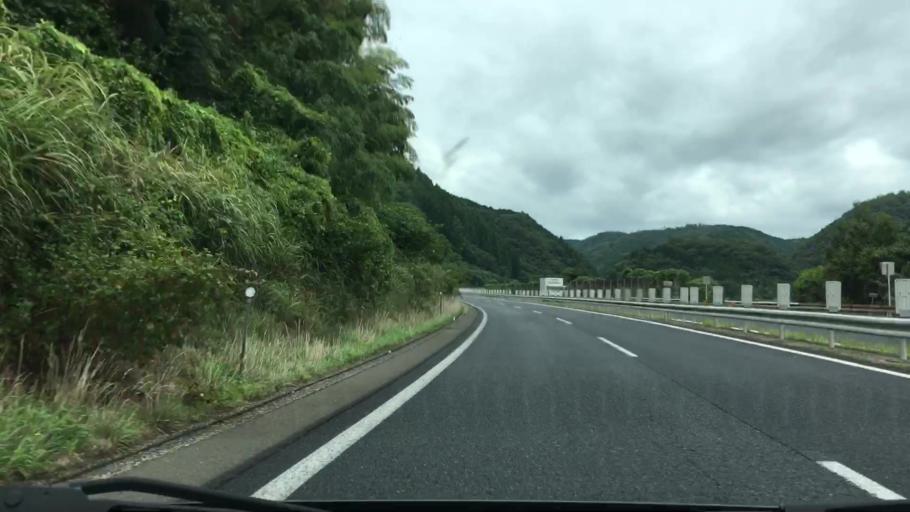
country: JP
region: Hyogo
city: Yamazakicho-nakabirose
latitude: 35.0111
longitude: 134.2916
